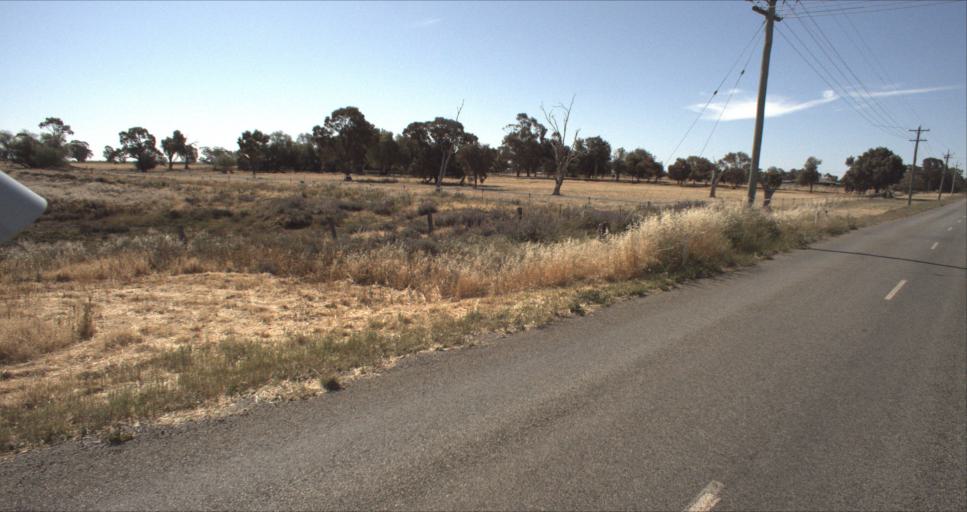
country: AU
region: New South Wales
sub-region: Leeton
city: Leeton
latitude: -34.5682
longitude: 146.3822
